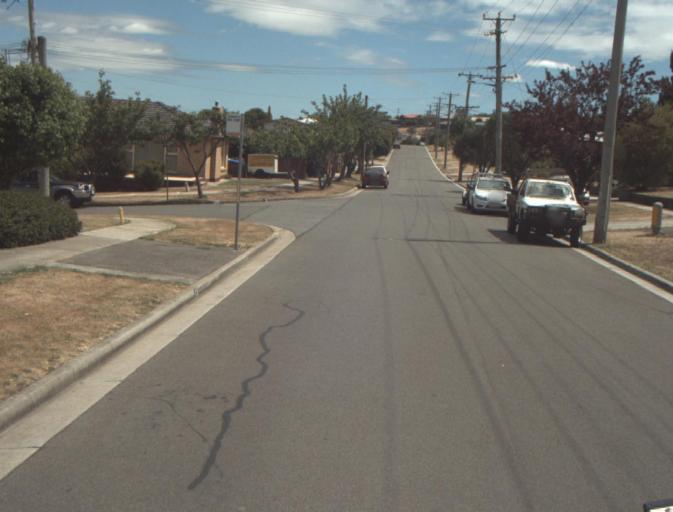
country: AU
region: Tasmania
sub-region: Launceston
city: Mayfield
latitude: -41.3855
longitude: 147.1214
